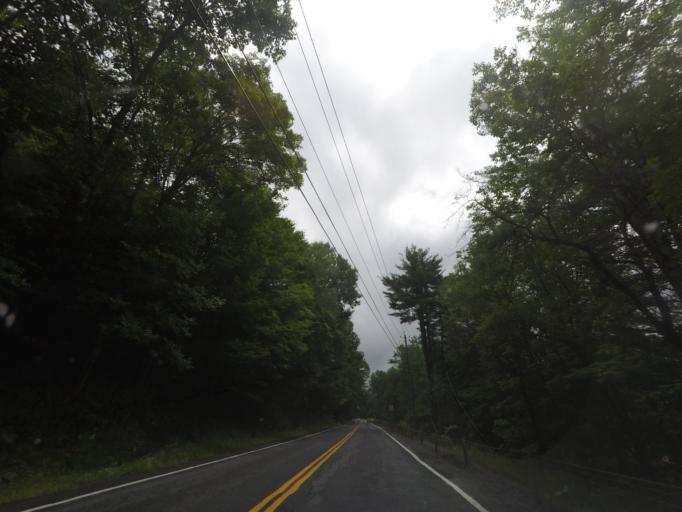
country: US
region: New York
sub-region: Rensselaer County
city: Averill Park
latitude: 42.5942
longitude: -73.5039
